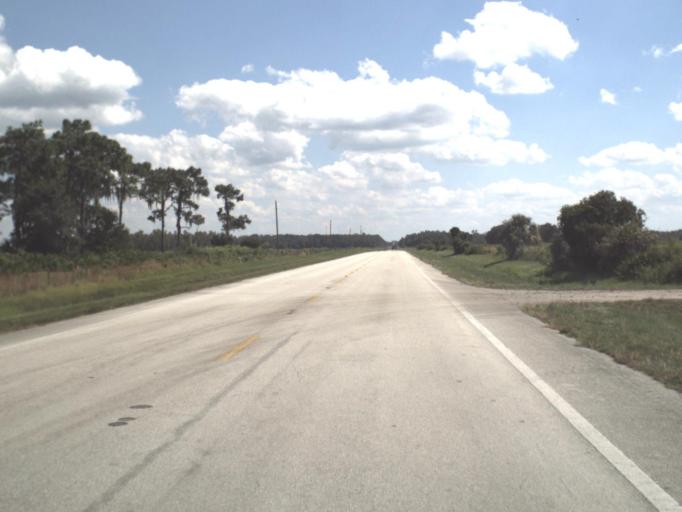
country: US
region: Florida
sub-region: Highlands County
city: Sebring
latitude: 27.4429
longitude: -81.6171
